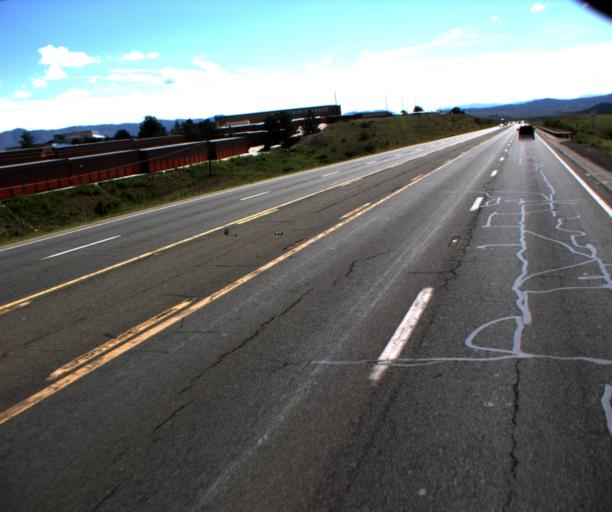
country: US
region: Arizona
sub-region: Yavapai County
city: Prescott Valley
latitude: 34.5830
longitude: -112.3088
